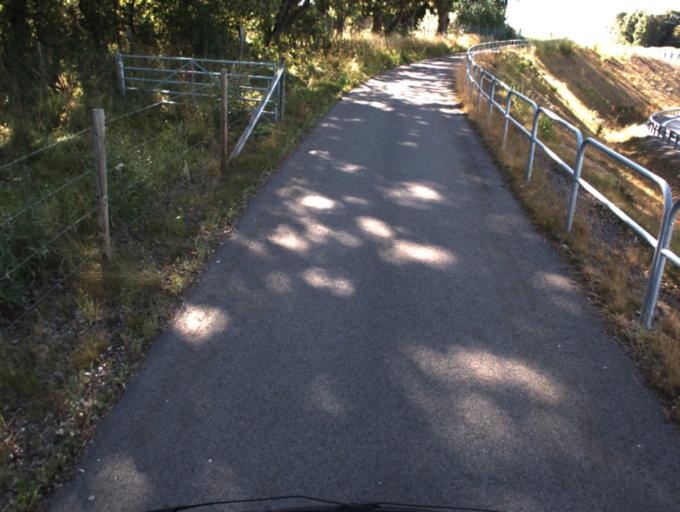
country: SE
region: Skane
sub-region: Helsingborg
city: Odakra
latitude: 56.0864
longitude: 12.7549
